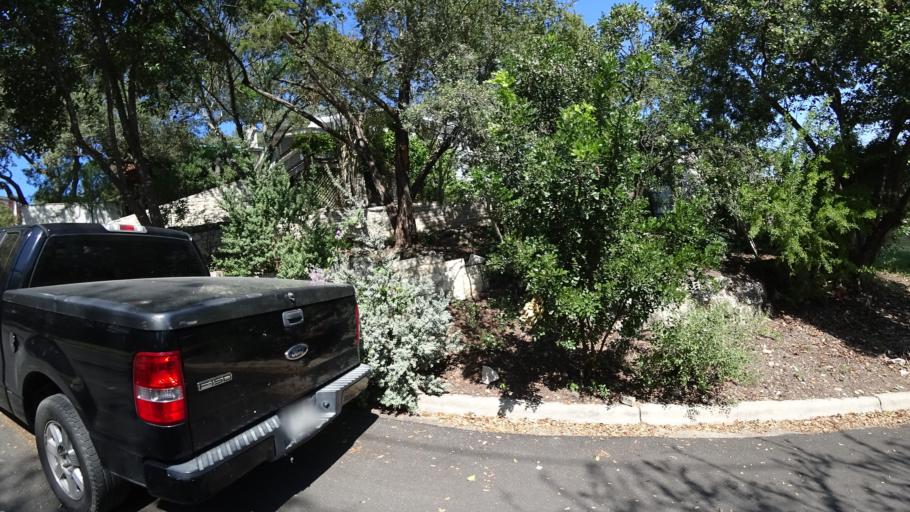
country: US
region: Texas
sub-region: Travis County
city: West Lake Hills
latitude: 30.2981
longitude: -97.7881
